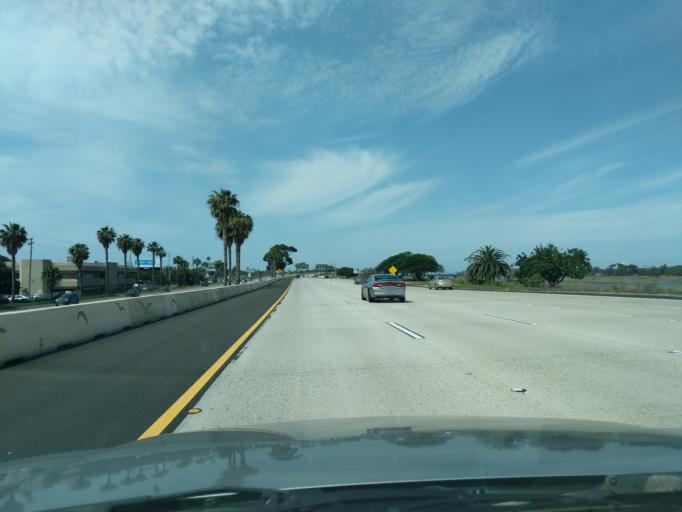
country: US
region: California
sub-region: San Diego County
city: San Diego
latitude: 32.7586
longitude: -117.2152
